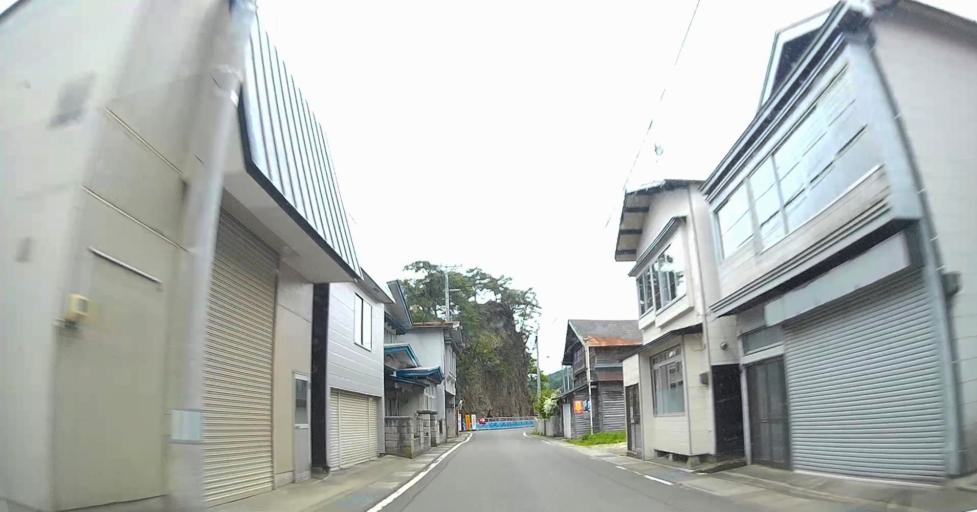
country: JP
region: Aomori
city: Shimokizukuri
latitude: 41.1998
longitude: 140.4299
